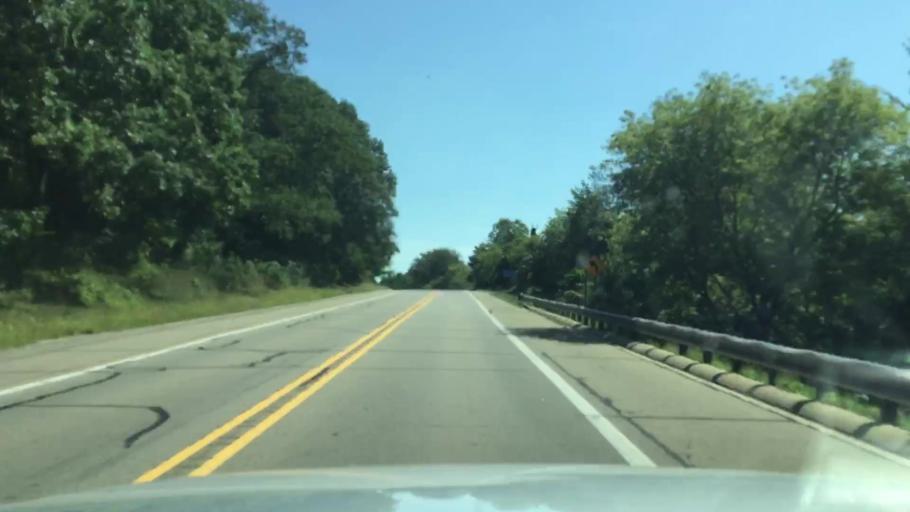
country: US
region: Michigan
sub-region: Jackson County
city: Brooklyn
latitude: 42.0579
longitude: -84.1750
